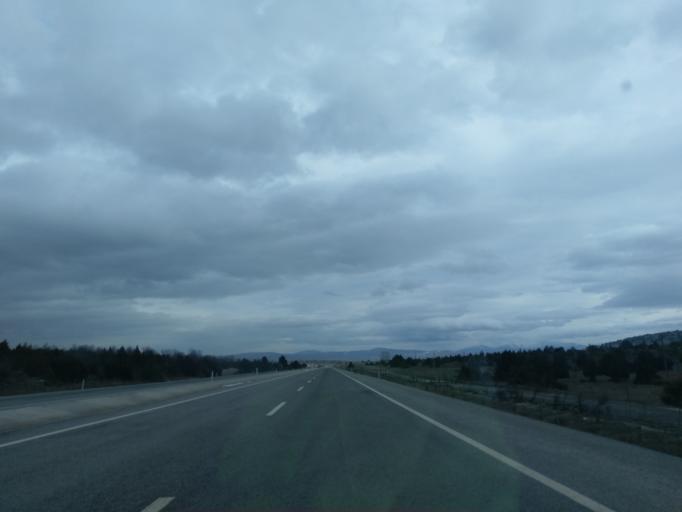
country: TR
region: Kuetahya
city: Aslanapa
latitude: 39.2282
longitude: 29.7627
